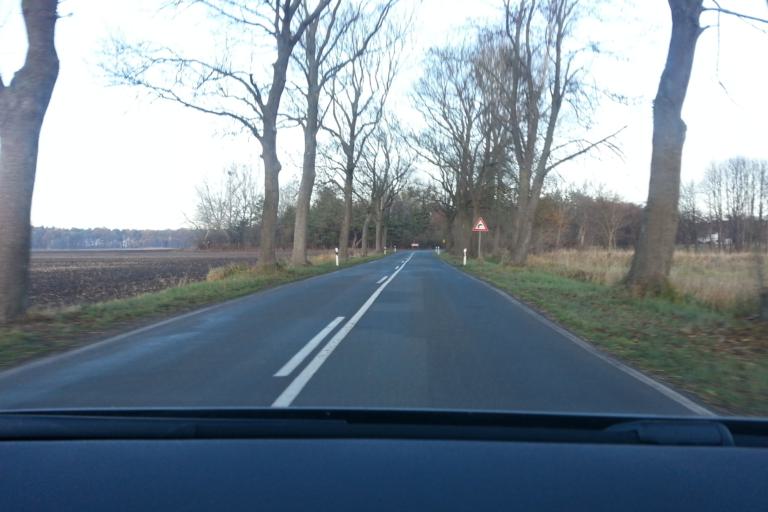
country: DE
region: Mecklenburg-Vorpommern
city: Ferdinandshof
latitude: 53.6525
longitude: 13.8713
